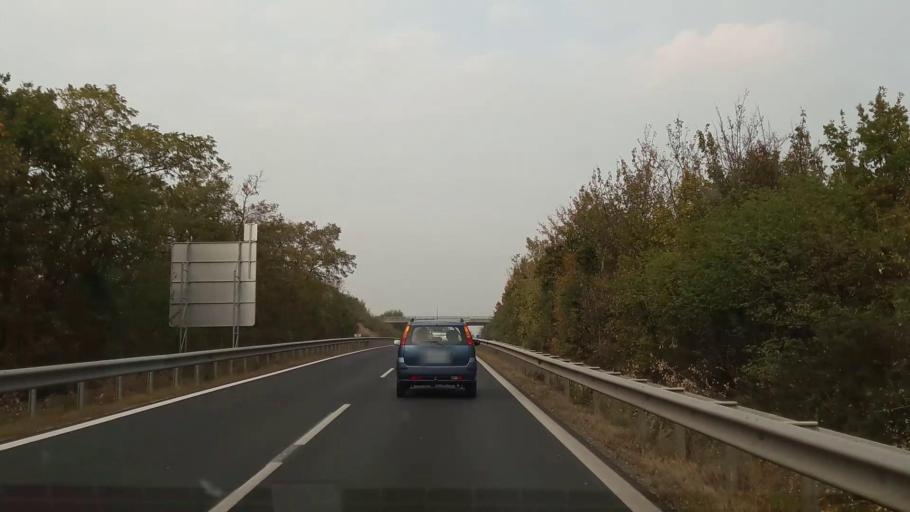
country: AT
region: Burgenland
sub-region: Politischer Bezirk Neusiedl am See
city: Weiden am See
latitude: 47.9134
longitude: 16.8900
